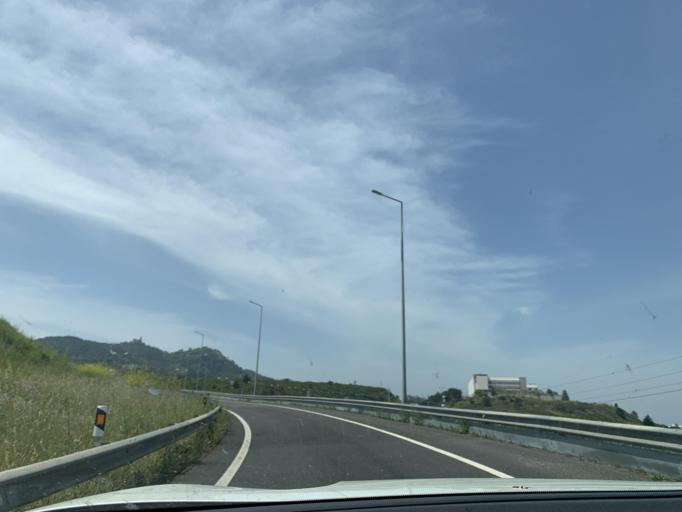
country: PT
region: Lisbon
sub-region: Sintra
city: Sintra
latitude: 38.8051
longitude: -9.3629
